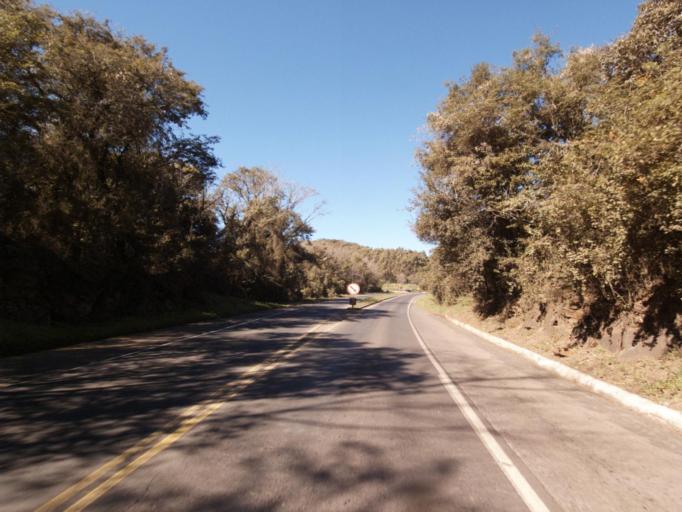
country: BR
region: Santa Catarina
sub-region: Chapeco
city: Chapeco
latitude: -26.9319
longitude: -52.8154
